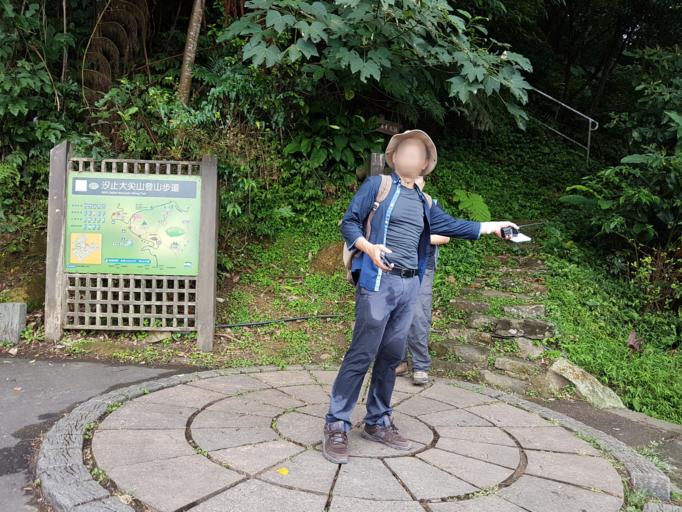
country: TW
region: Taiwan
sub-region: Keelung
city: Keelung
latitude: 25.0505
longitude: 121.6654
